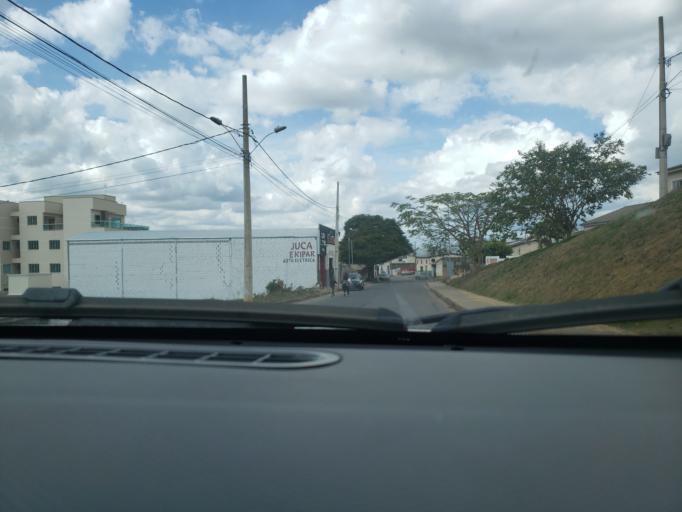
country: BR
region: Minas Gerais
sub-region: Campo Belo
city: Campo Belo
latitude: -20.9054
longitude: -45.2825
